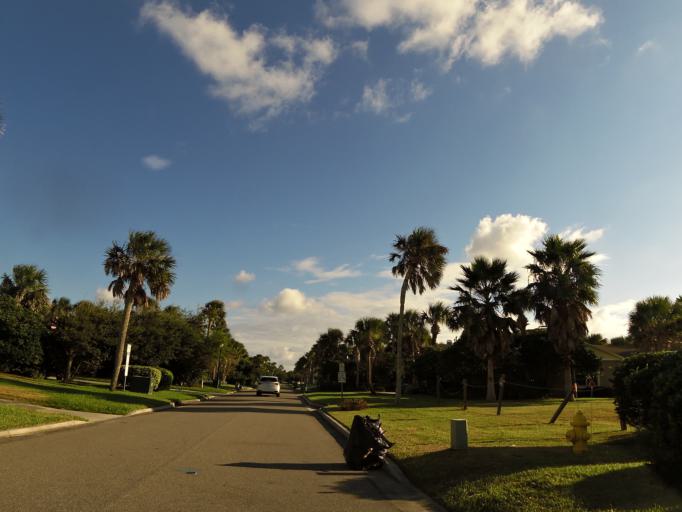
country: US
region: Florida
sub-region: Saint Johns County
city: Ponte Vedra Beach
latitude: 30.2561
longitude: -81.3825
